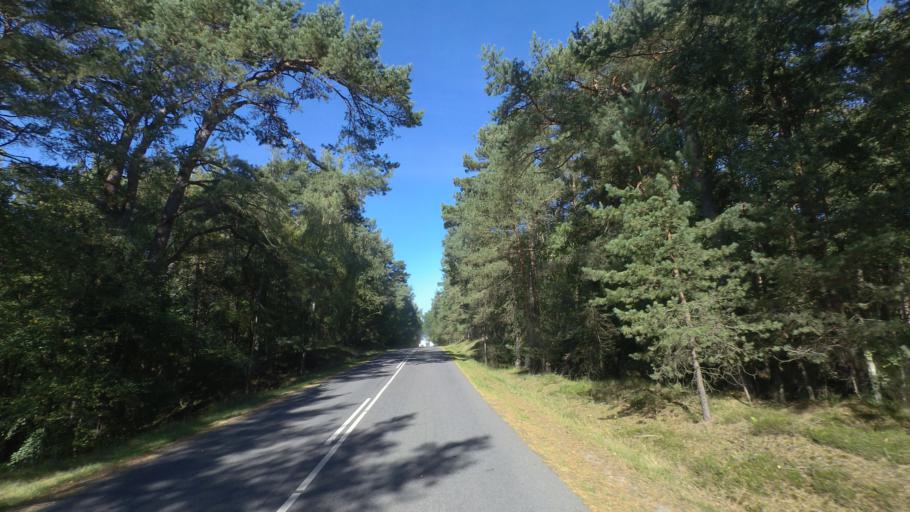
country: DK
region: Capital Region
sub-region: Bornholm Kommune
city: Nexo
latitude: 54.9992
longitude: 15.0758
